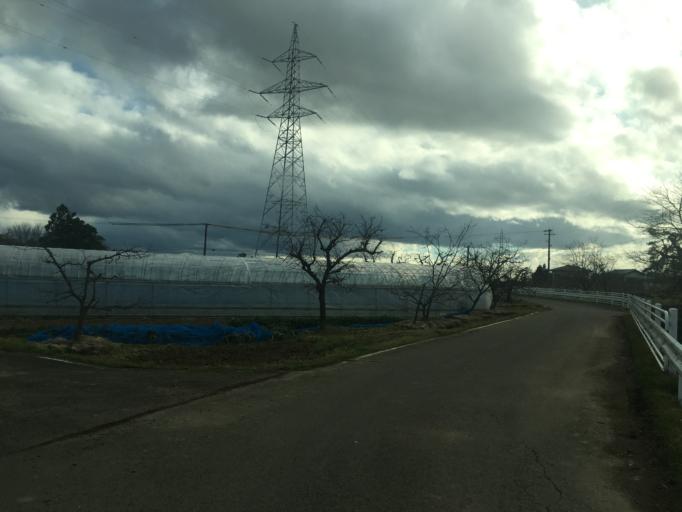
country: JP
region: Fukushima
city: Yanagawamachi-saiwaicho
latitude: 37.8897
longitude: 140.5789
